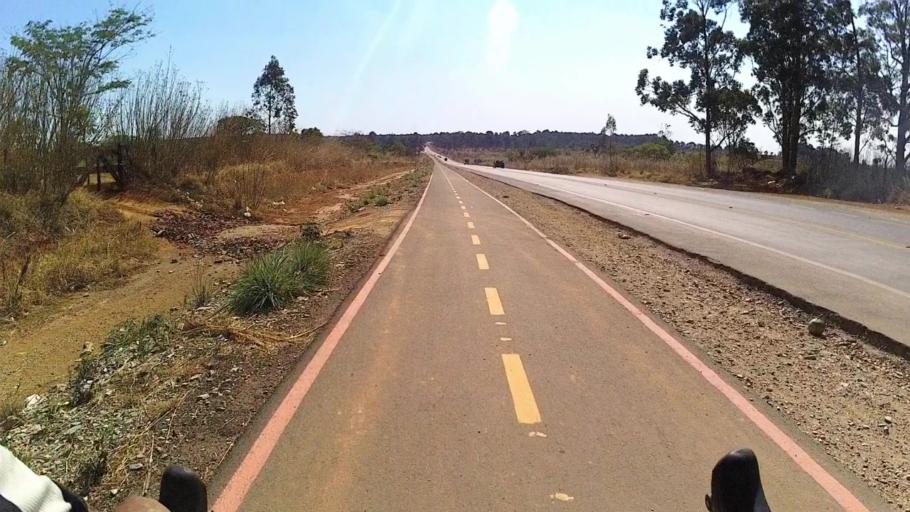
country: BR
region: Federal District
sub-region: Brasilia
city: Brasilia
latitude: -15.6790
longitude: -48.2356
